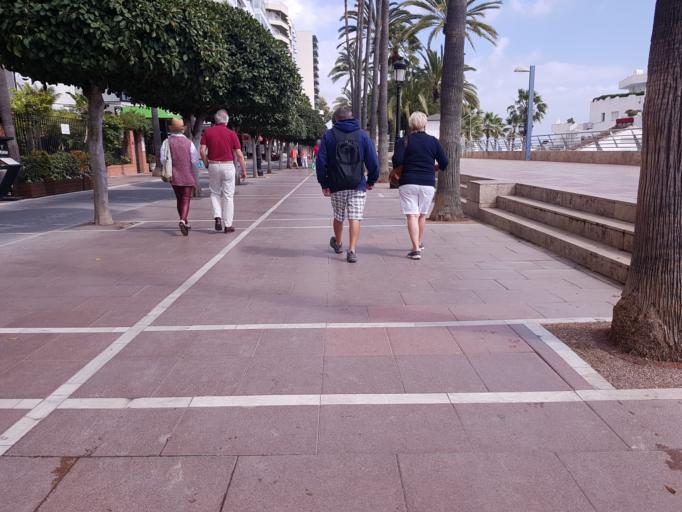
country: ES
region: Andalusia
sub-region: Provincia de Malaga
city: Marbella
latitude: 36.5071
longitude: -4.8886
